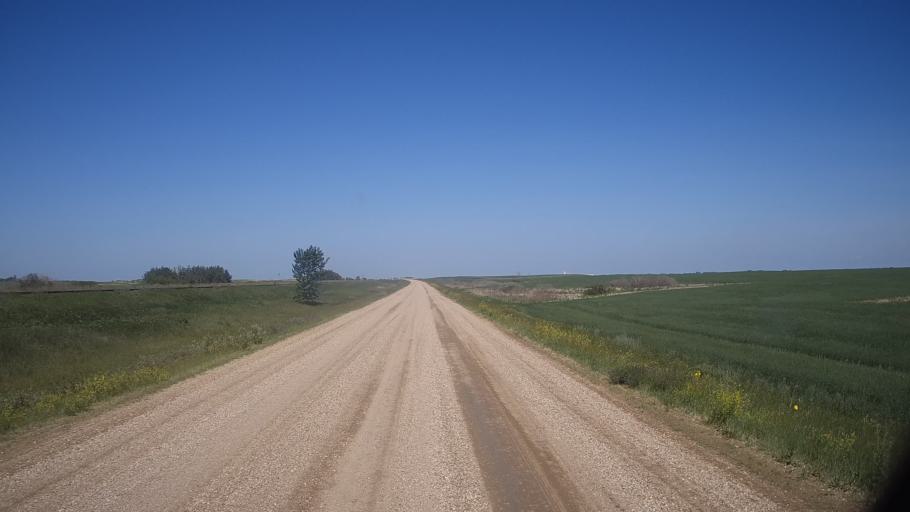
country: CA
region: Saskatchewan
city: Watrous
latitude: 51.8434
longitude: -105.9146
